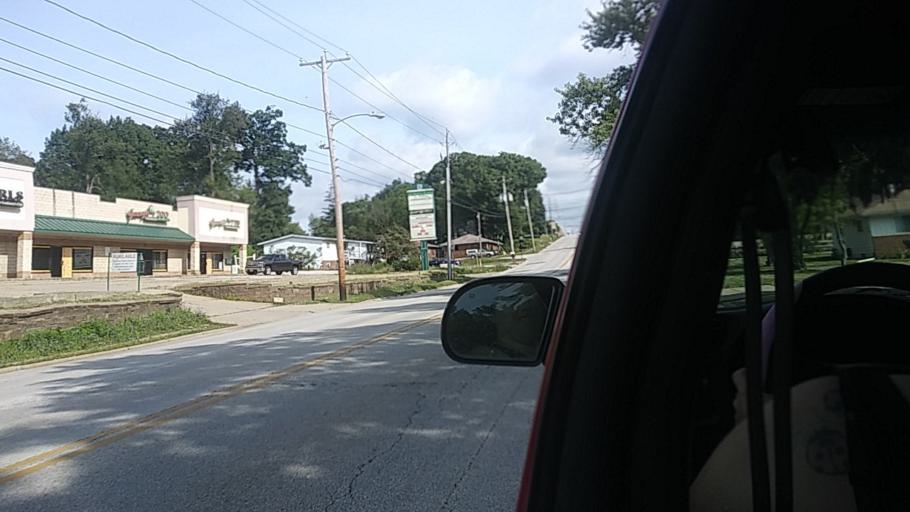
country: US
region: Ohio
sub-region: Summit County
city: Tallmadge
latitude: 41.0981
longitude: -81.4664
